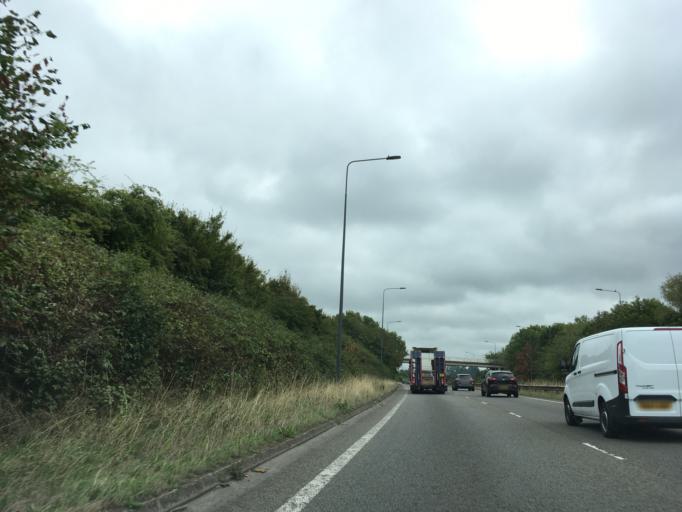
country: GB
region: England
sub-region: South Gloucestershire
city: Mangotsfield
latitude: 51.4962
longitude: -2.4763
